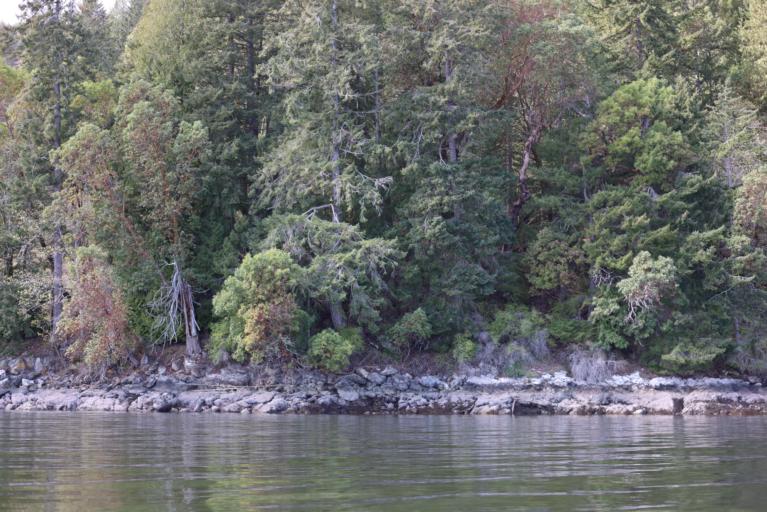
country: CA
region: British Columbia
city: North Saanich
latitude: 48.5916
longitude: -123.5206
